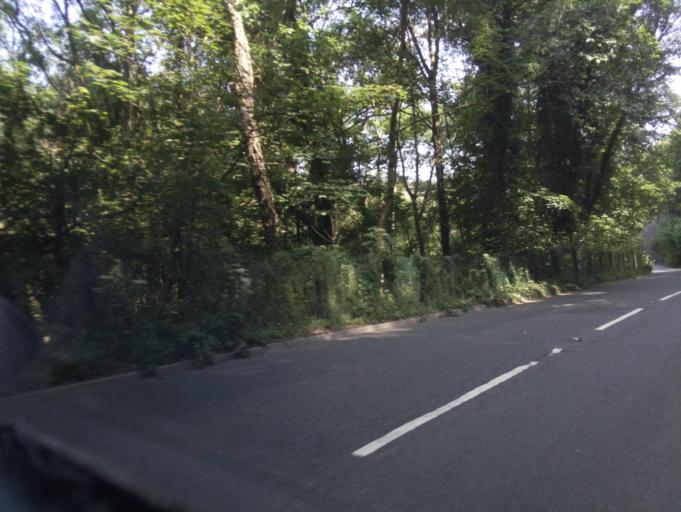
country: GB
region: Wales
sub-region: Caerphilly County Borough
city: Bargoed
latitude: 51.6951
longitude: -3.2330
